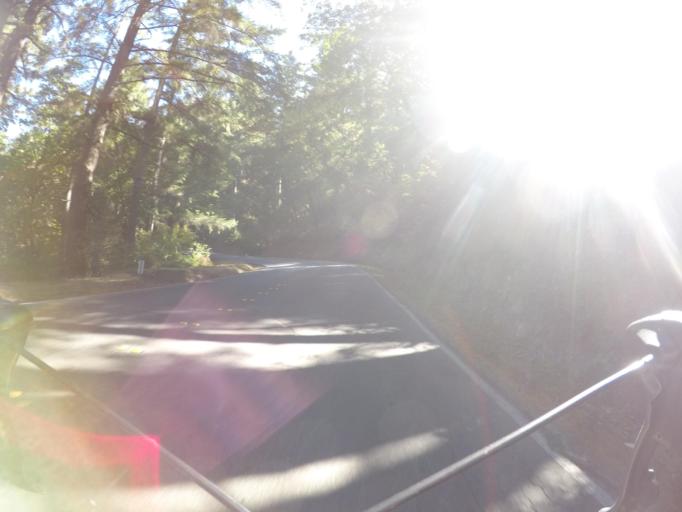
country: US
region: California
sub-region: San Mateo County
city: Portola Valley
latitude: 37.2896
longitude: -122.2791
